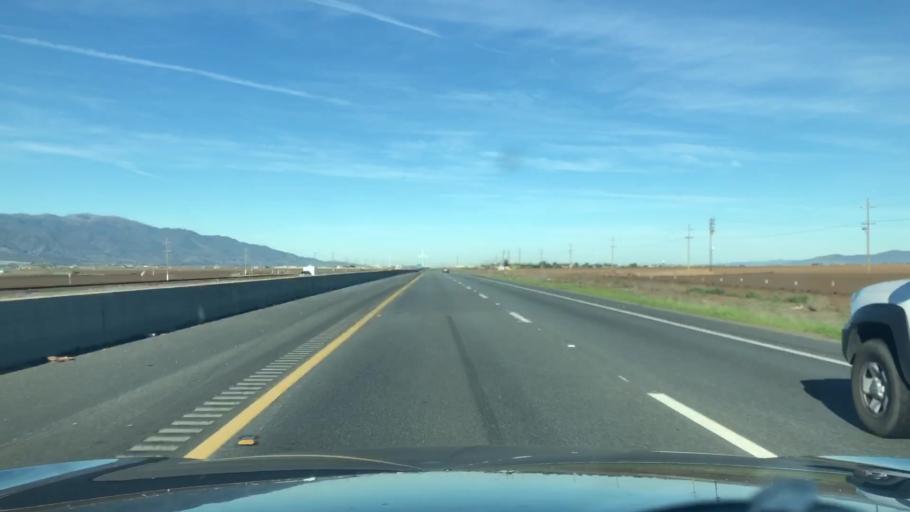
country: US
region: California
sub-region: Monterey County
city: Gonzales
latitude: 36.4761
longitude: -121.4058
